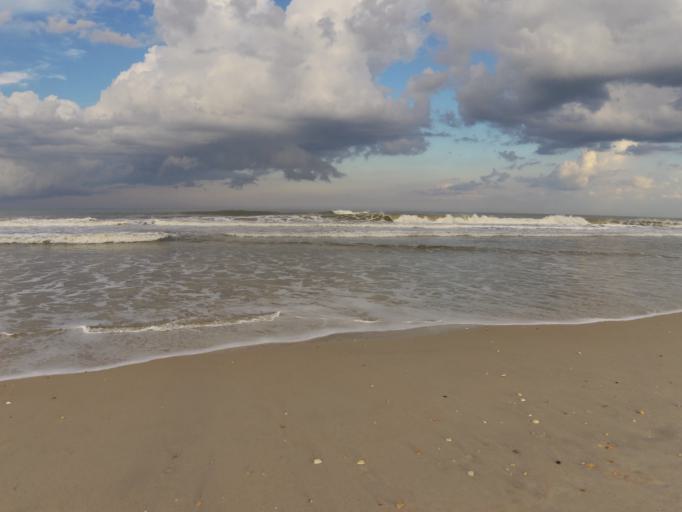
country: US
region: Florida
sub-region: Saint Johns County
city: Villano Beach
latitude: 29.9706
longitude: -81.3095
